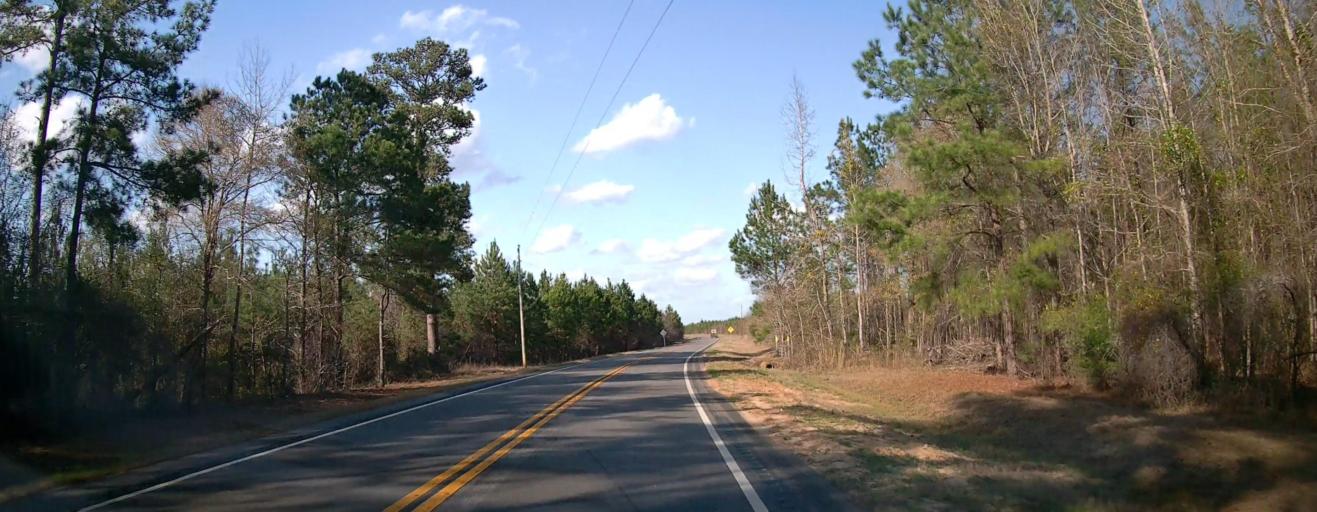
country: US
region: Georgia
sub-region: Wheeler County
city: Alamo
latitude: 32.0688
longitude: -82.8135
